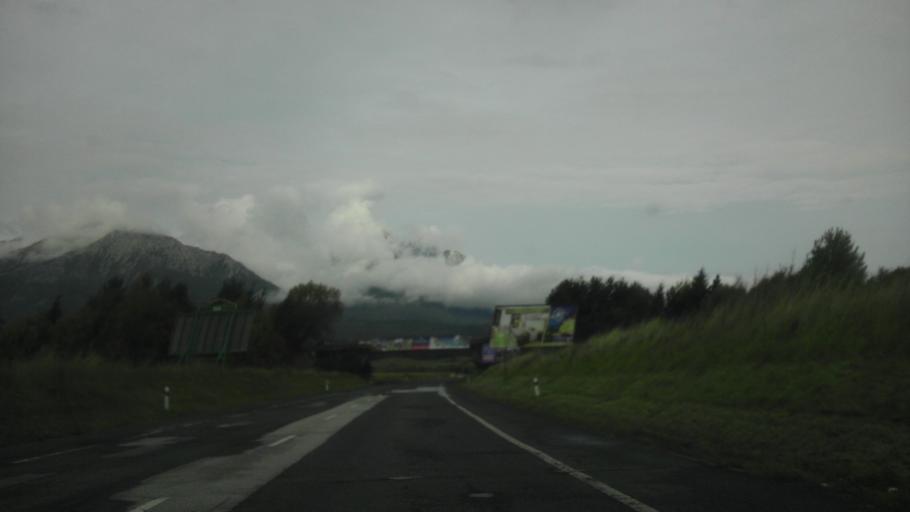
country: SK
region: Presovsky
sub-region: Okres Poprad
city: Nova Lesna
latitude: 49.0917
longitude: 20.2611
